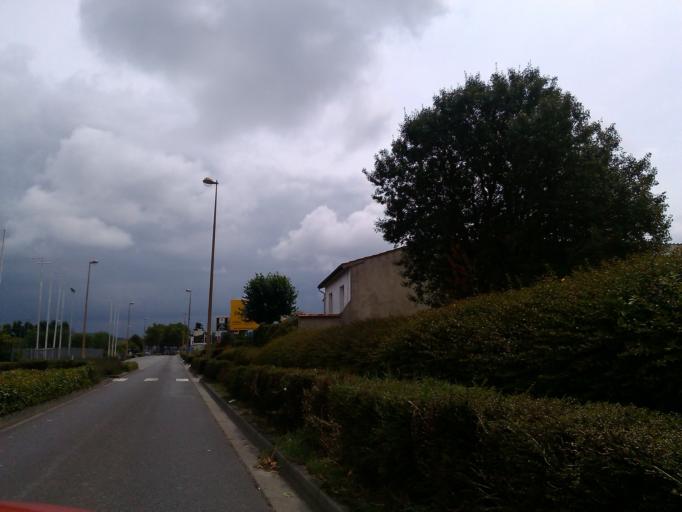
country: FR
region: Poitou-Charentes
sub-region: Departement de la Charente
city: Saint-Brice
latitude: 45.6842
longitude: -0.3006
